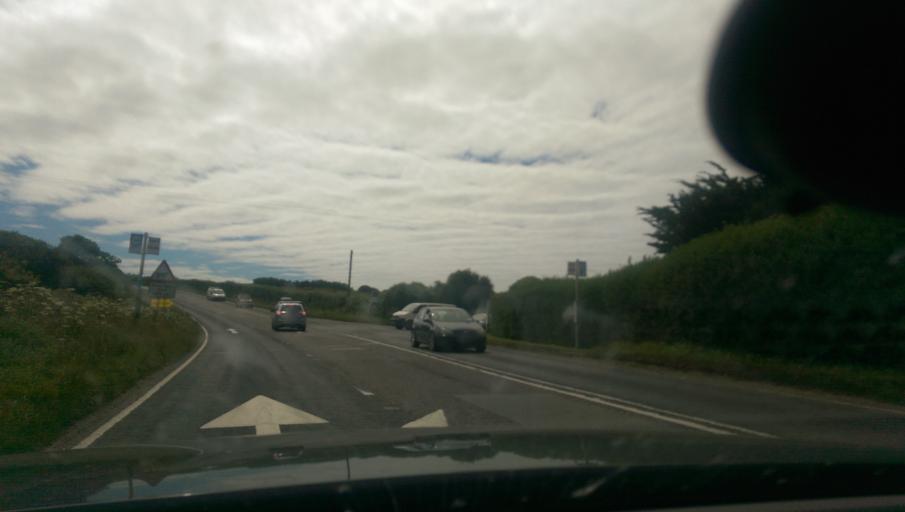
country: GB
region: England
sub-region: Cornwall
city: Wadebridge
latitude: 50.5081
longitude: -4.8815
